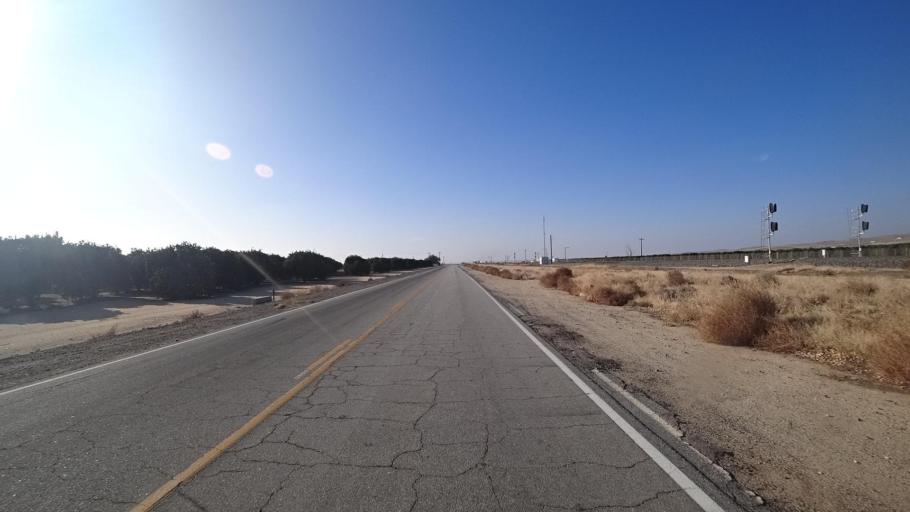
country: US
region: California
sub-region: Kern County
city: Arvin
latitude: 35.3273
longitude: -118.7859
